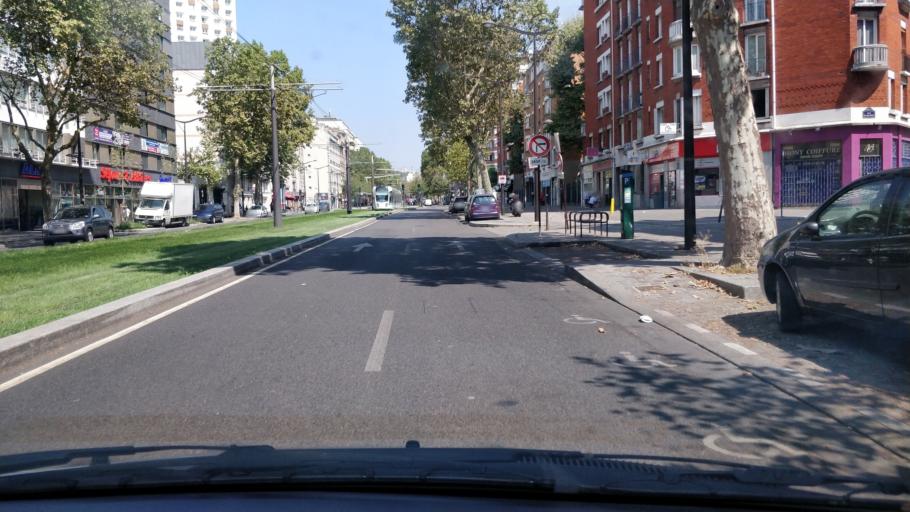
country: FR
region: Ile-de-France
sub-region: Departement de Seine-Saint-Denis
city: Bagnolet
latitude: 48.8573
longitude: 2.4101
